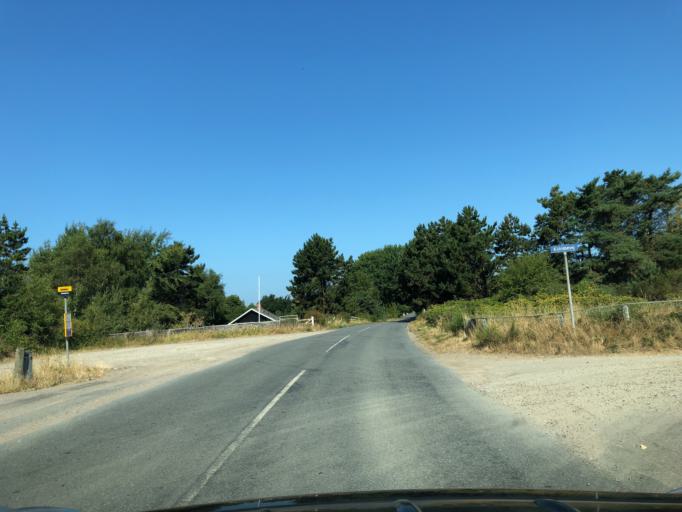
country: DK
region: Zealand
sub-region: Odsherred Kommune
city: Asnaes
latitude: 55.9842
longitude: 11.3041
